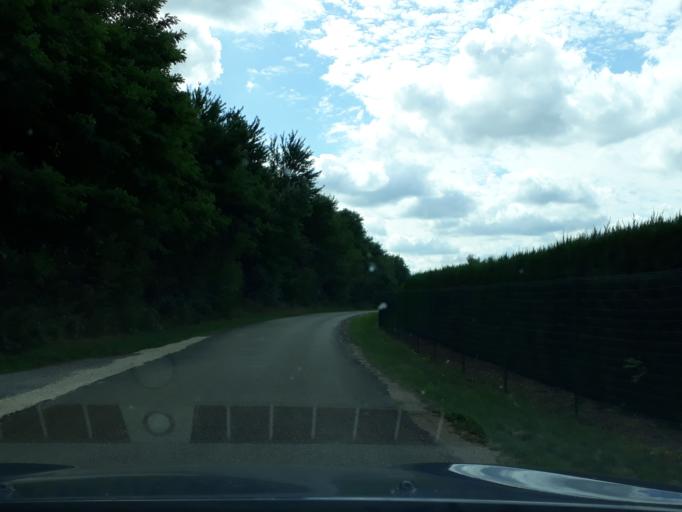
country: FR
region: Centre
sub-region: Departement du Loiret
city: Saint-Cyr-en-Val
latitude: 47.8501
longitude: 1.9762
